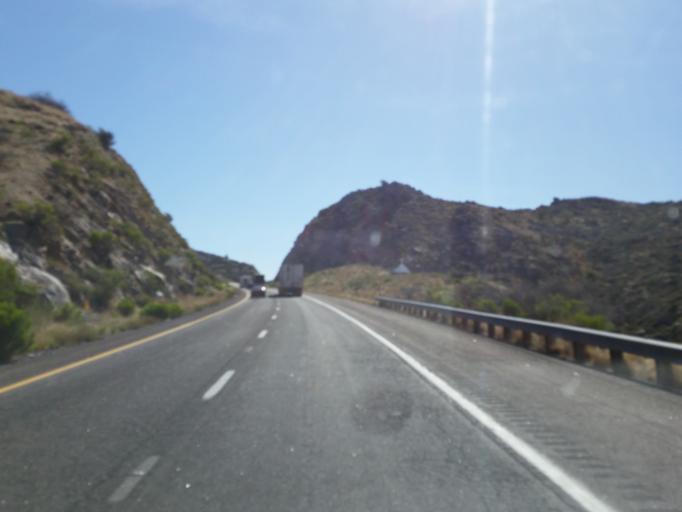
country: US
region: Arizona
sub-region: Mohave County
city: Peach Springs
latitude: 35.1708
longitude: -113.5116
